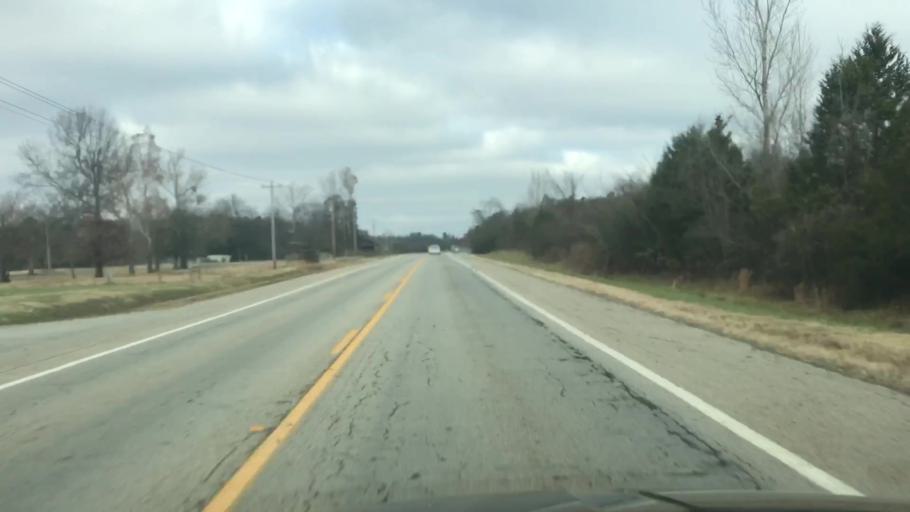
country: US
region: Arkansas
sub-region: Scott County
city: Waldron
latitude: 34.8498
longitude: -94.0612
